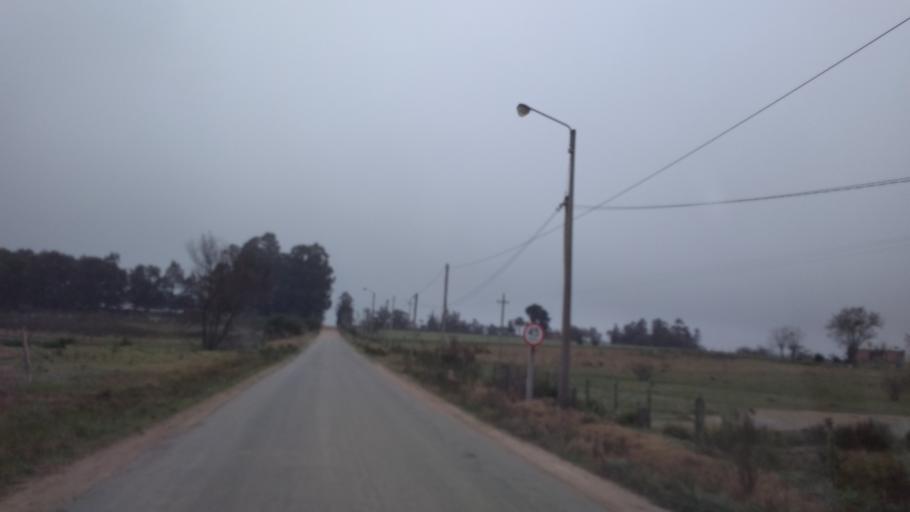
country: UY
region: Florida
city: Florida
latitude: -34.0820
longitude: -56.2042
